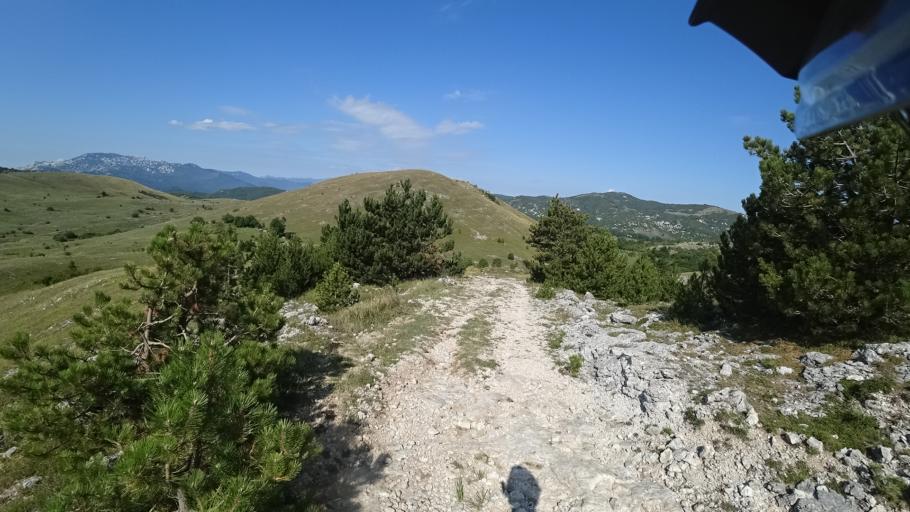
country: HR
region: Zadarska
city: Gracac
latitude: 44.3020
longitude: 15.9664
